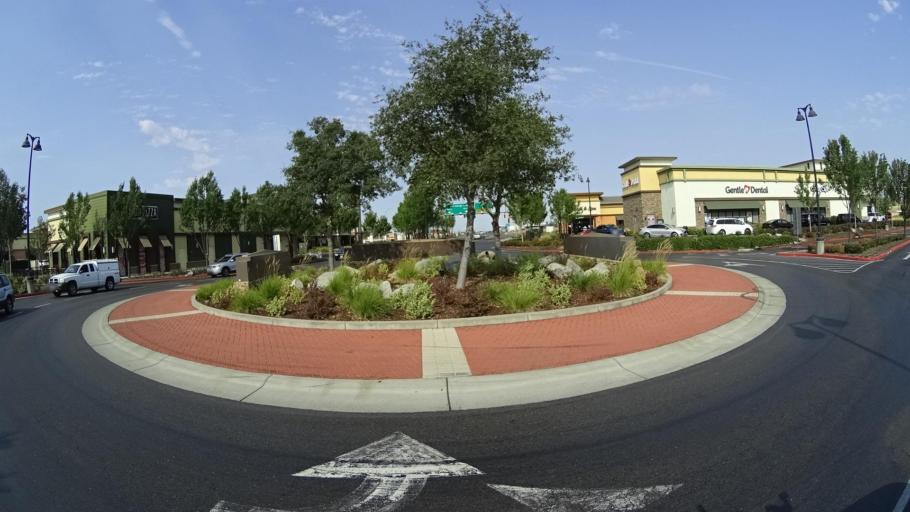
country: US
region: California
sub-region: Placer County
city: Loomis
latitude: 38.8007
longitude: -121.2035
